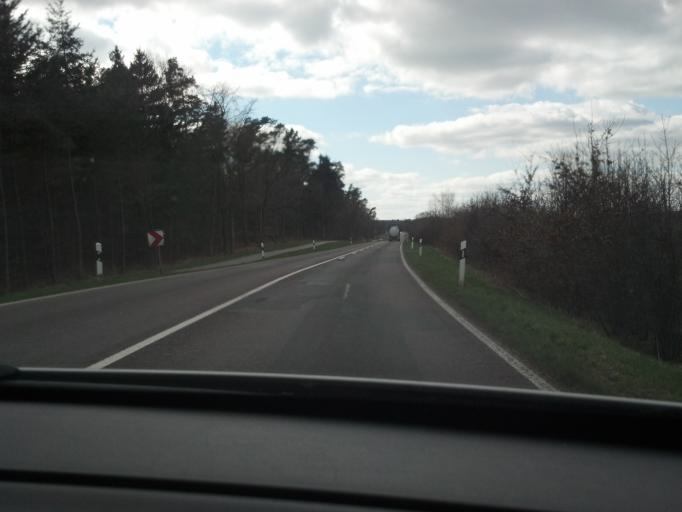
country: DE
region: Mecklenburg-Vorpommern
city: Malchow
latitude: 53.3647
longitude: 12.4486
